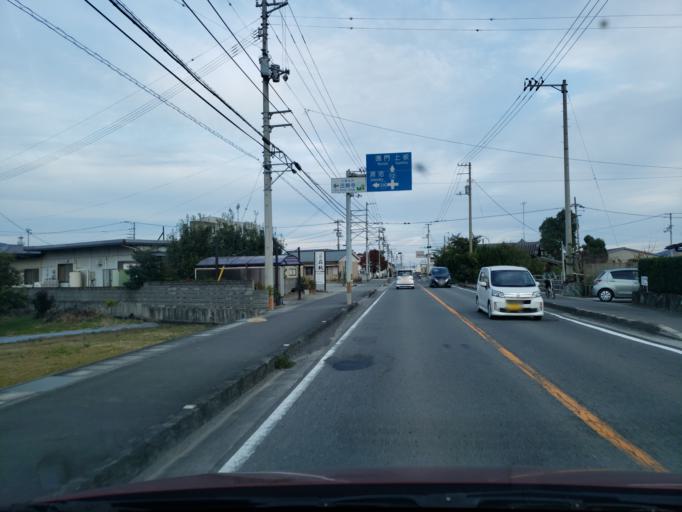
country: JP
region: Tokushima
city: Kamojimacho-jogejima
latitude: 34.1003
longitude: 134.3371
